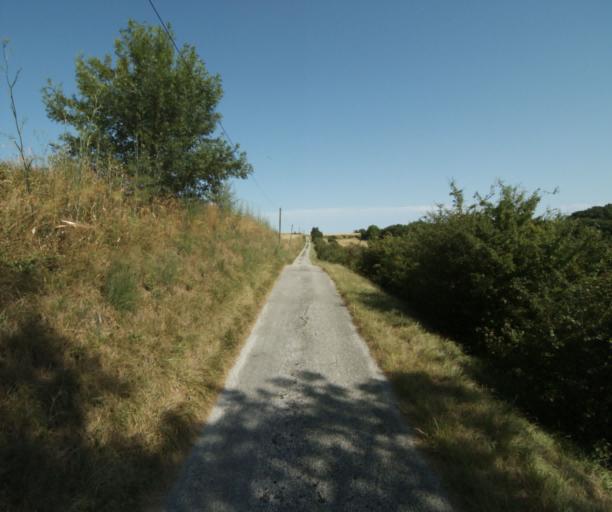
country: FR
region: Midi-Pyrenees
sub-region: Departement de la Haute-Garonne
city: Saint-Felix-Lauragais
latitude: 43.4313
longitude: 1.8441
